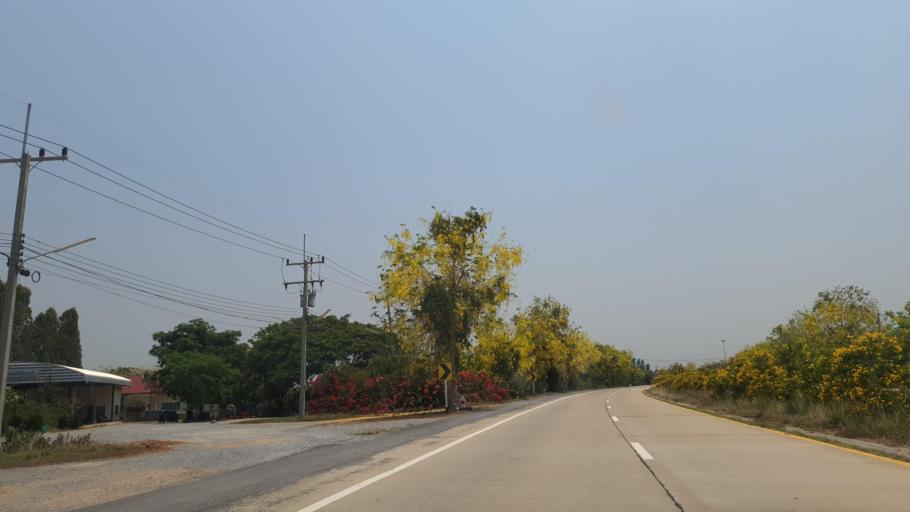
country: TH
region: Suphan Buri
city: Suphan Buri
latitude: 14.5384
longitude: 100.0660
